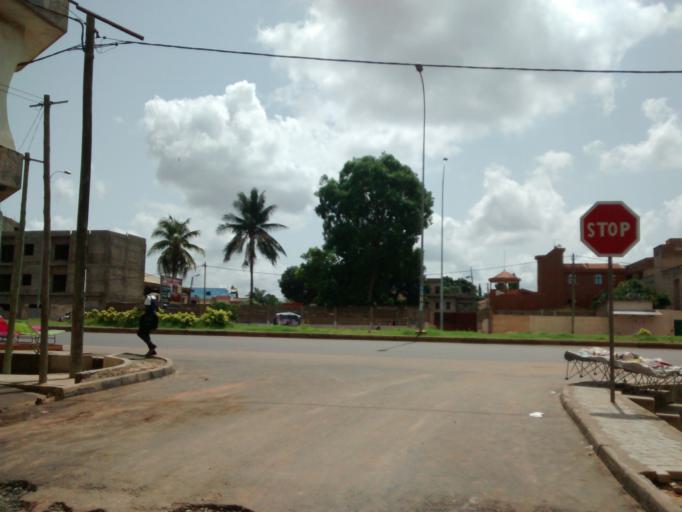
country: TG
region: Maritime
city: Lome
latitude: 6.2043
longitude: 1.1902
